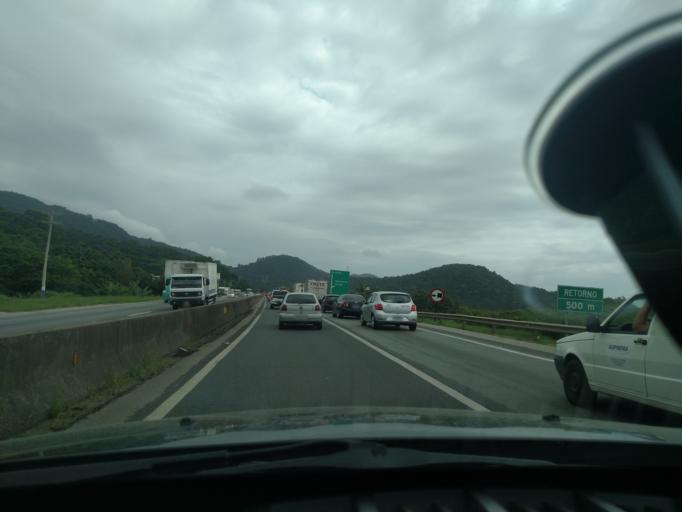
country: BR
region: Santa Catarina
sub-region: Itapema
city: Itapema
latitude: -27.0694
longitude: -48.5955
